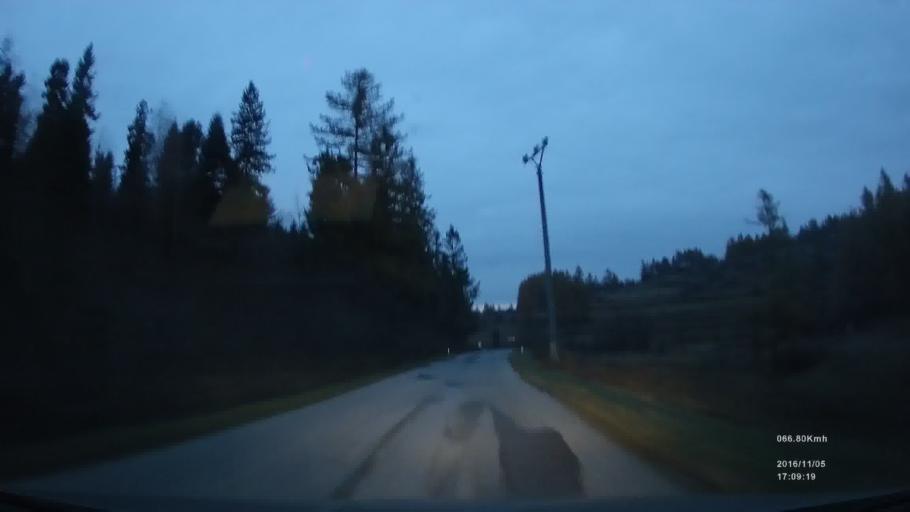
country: SK
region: Presovsky
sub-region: Okres Presov
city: Levoca
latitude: 49.0535
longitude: 20.5159
